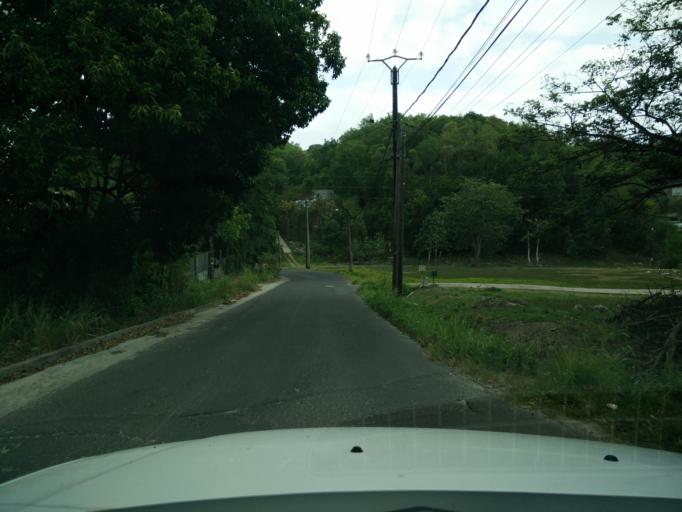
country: GP
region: Guadeloupe
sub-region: Guadeloupe
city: Le Gosier
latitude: 16.2283
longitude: -61.4416
